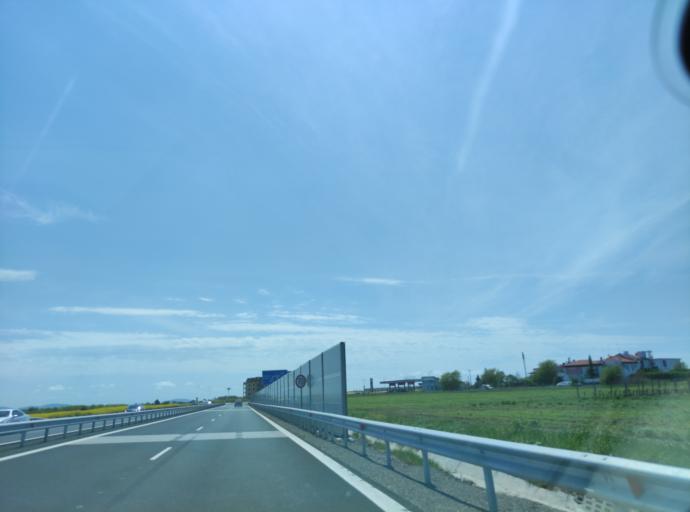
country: BG
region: Burgas
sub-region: Obshtina Pomorie
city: Pomorie
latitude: 42.5633
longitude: 27.5709
